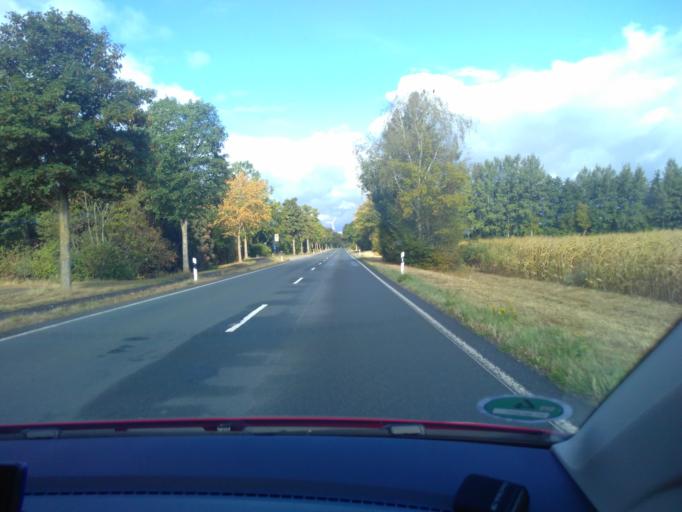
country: DE
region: North Rhine-Westphalia
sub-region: Regierungsbezirk Munster
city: Ostbevern
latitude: 52.0149
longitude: 7.9110
